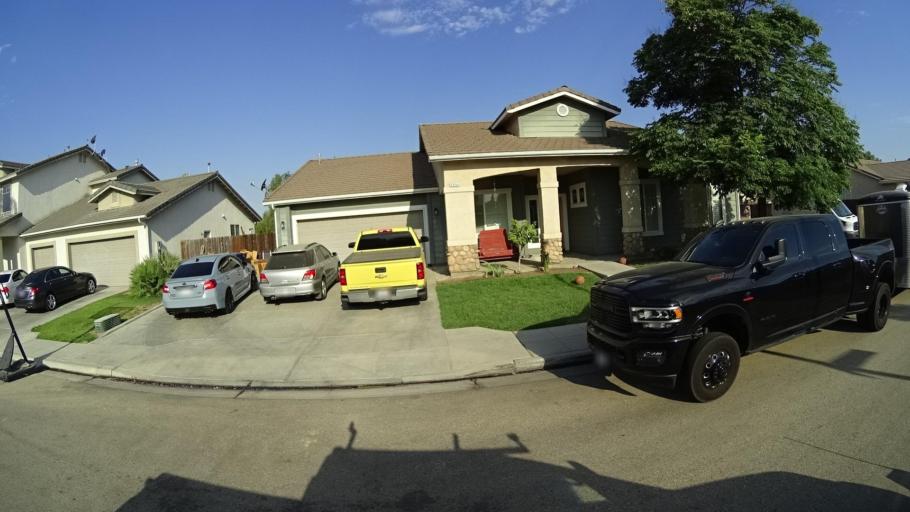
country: US
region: California
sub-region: Fresno County
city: Sunnyside
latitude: 36.7092
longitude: -119.6928
